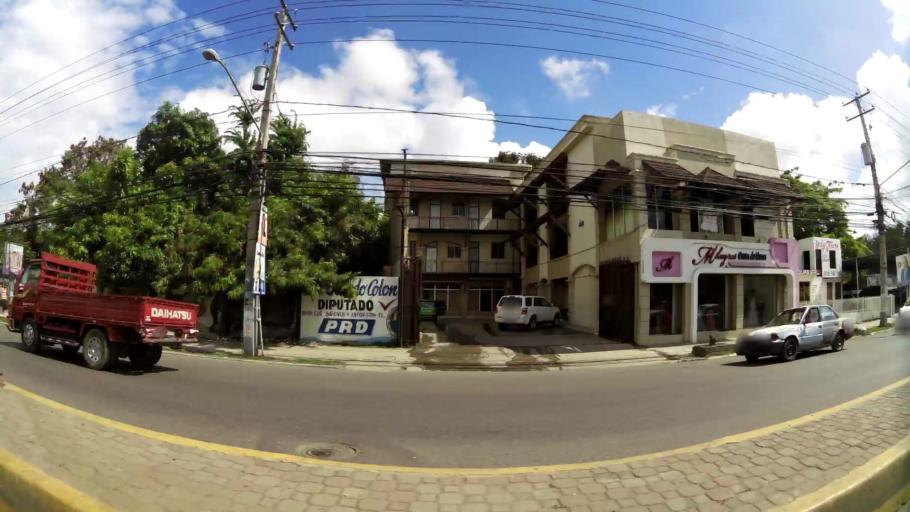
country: DO
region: Santiago
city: Santiago de los Caballeros
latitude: 19.4701
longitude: -70.6885
